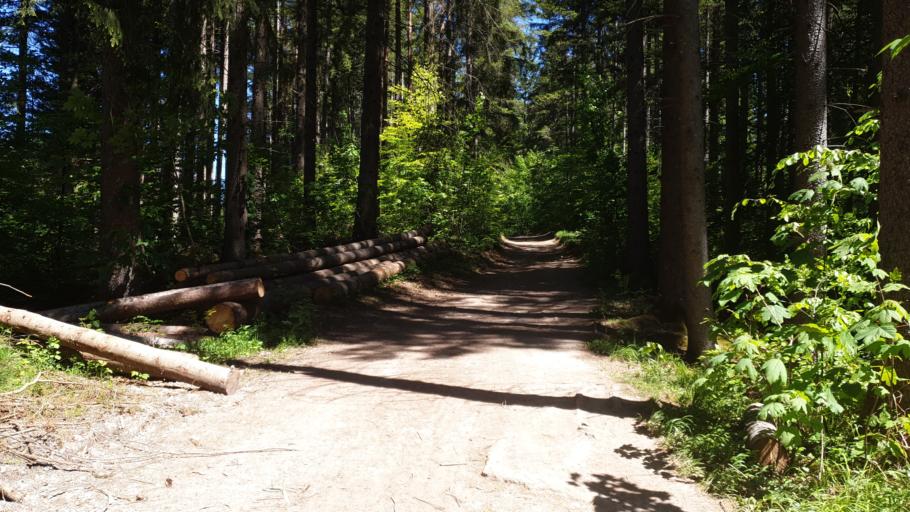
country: DE
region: Bavaria
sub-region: Upper Bavaria
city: Iffeldorf
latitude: 47.7805
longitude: 11.3004
